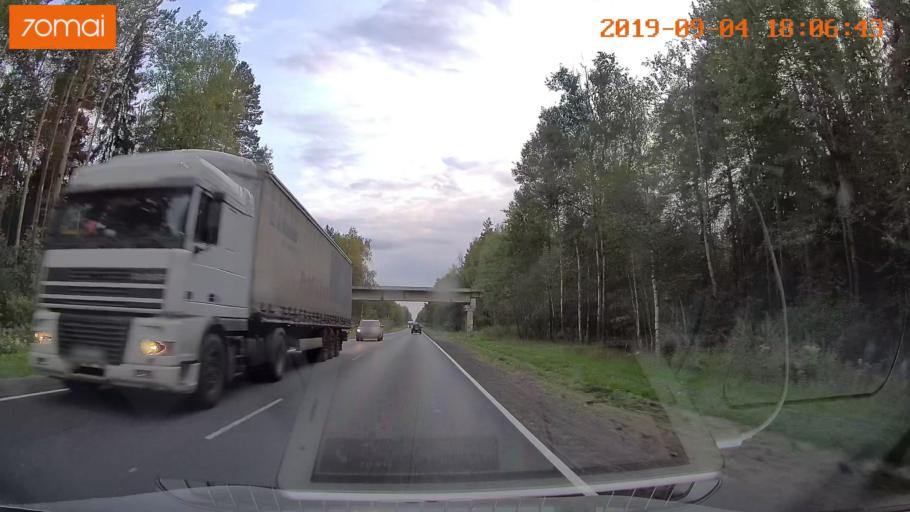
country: RU
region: Moskovskaya
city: Khorlovo
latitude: 55.4280
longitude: 38.8112
